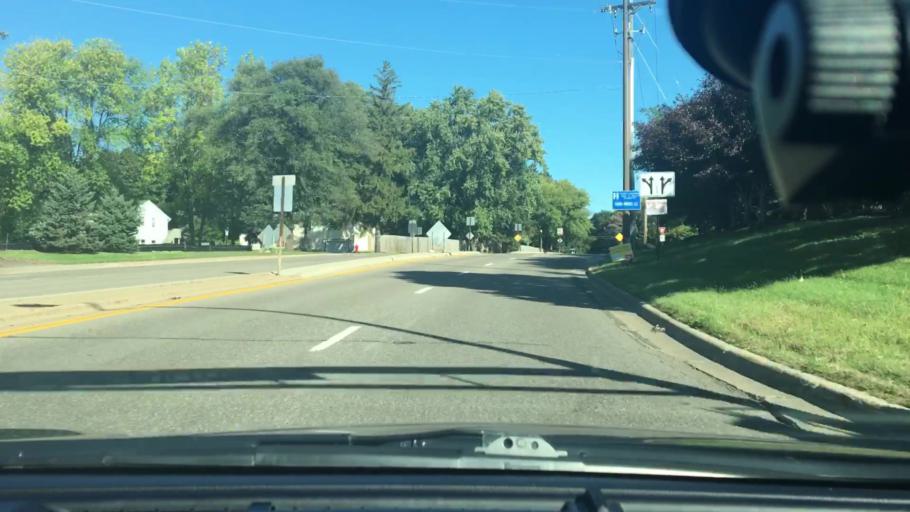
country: US
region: Minnesota
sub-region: Hennepin County
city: Minnetonka Mills
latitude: 44.9731
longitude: -93.4462
